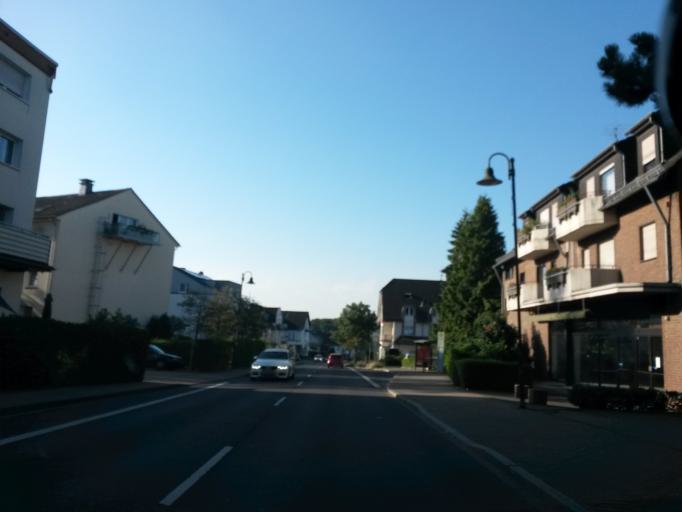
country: DE
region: North Rhine-Westphalia
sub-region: Regierungsbezirk Koln
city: Rosrath
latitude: 50.9186
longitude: 7.1745
